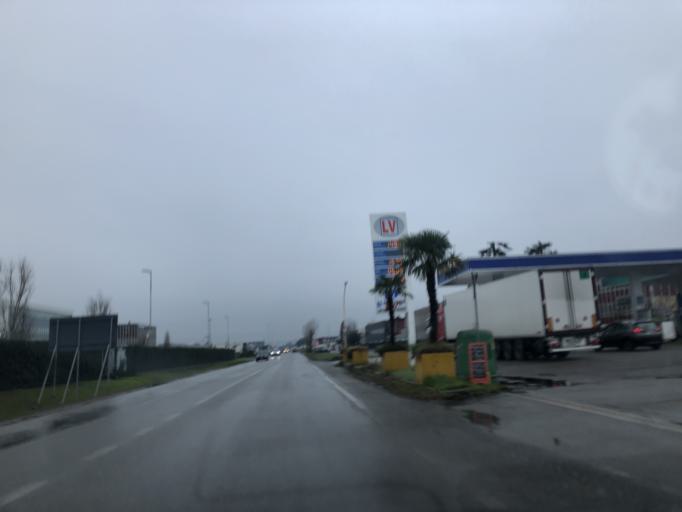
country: IT
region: Emilia-Romagna
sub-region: Provincia di Modena
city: Modena
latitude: 44.6568
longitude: 10.8823
